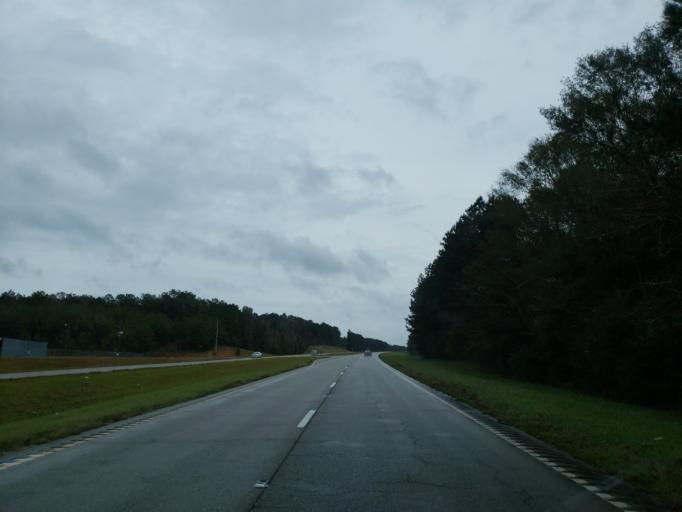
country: US
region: Mississippi
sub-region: Jones County
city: Laurel
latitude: 31.7058
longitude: -89.0689
